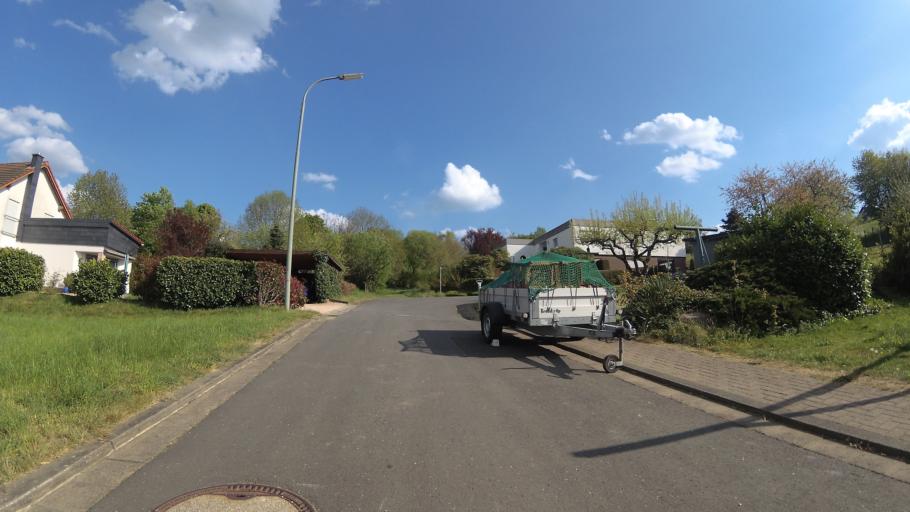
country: DE
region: Rheinland-Pfalz
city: Selchenbach
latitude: 49.4891
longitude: 7.2657
